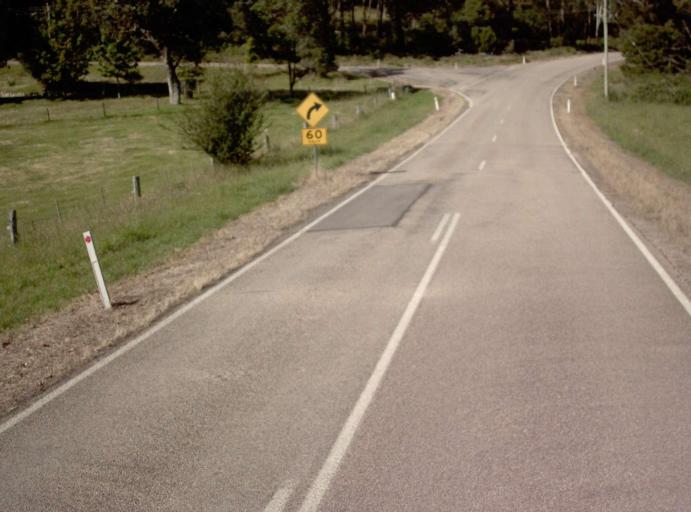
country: AU
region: Victoria
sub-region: East Gippsland
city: Lakes Entrance
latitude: -37.7421
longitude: 147.8171
